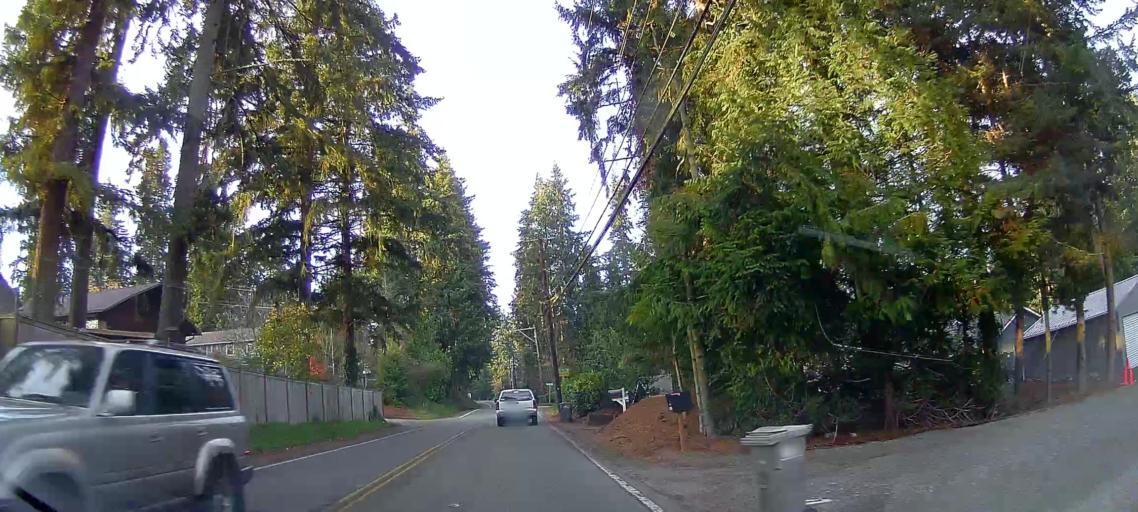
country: US
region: Washington
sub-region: Snohomish County
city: Alderwood Manor
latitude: 47.8178
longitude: -122.2577
